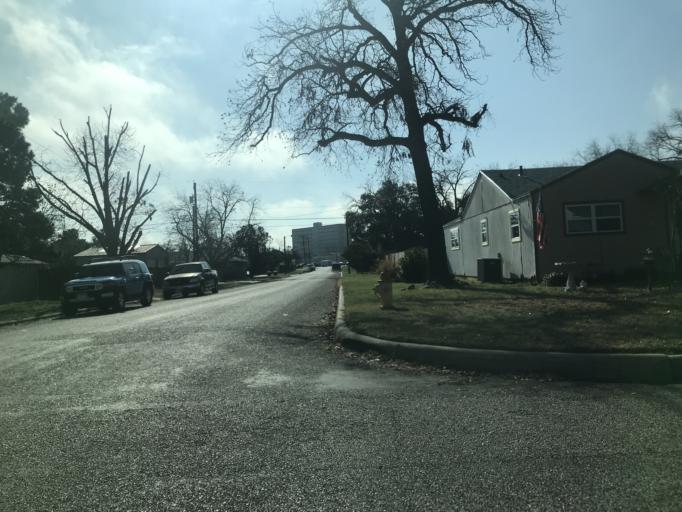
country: US
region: Texas
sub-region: Tom Green County
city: San Angelo
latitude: 31.4448
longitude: -100.4616
